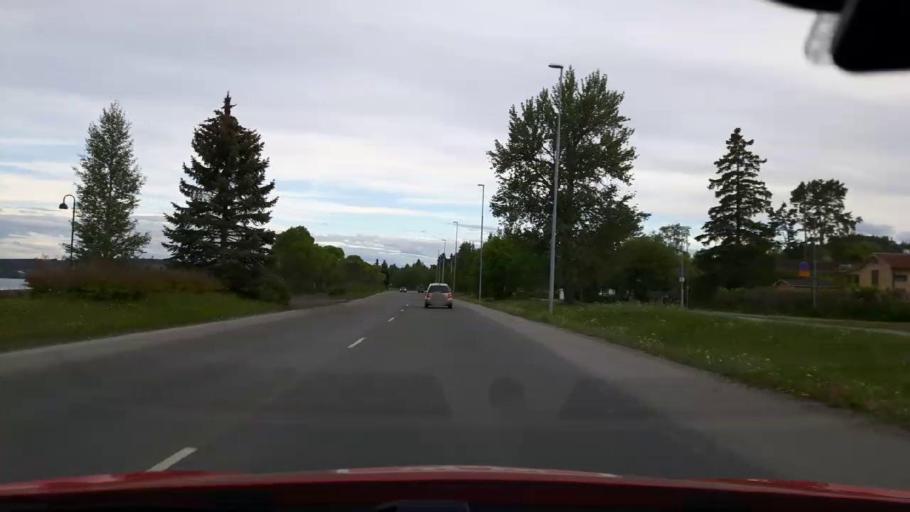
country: SE
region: Jaemtland
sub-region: OEstersunds Kommun
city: Ostersund
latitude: 63.1764
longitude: 14.6132
